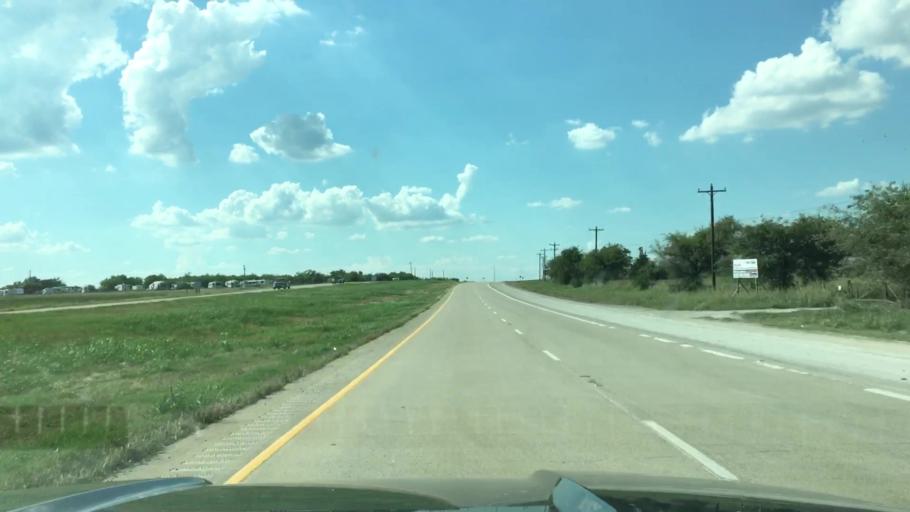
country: US
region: Texas
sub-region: Wise County
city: Rhome
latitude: 33.0409
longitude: -97.4470
